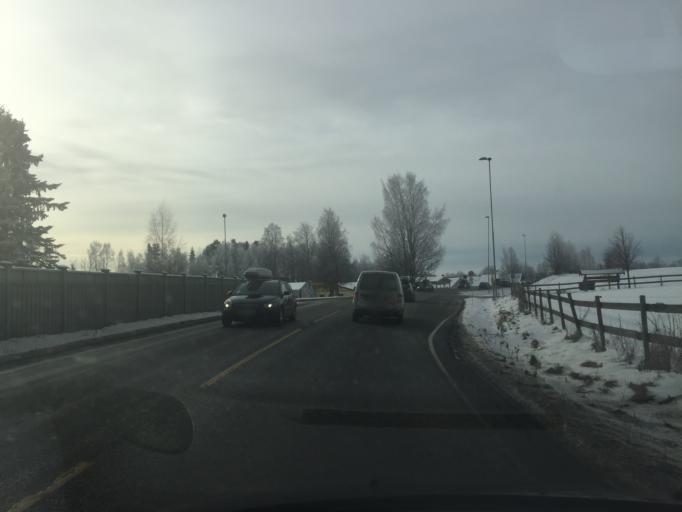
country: NO
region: Hedmark
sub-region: Loten
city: Loten
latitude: 60.8264
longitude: 11.3467
